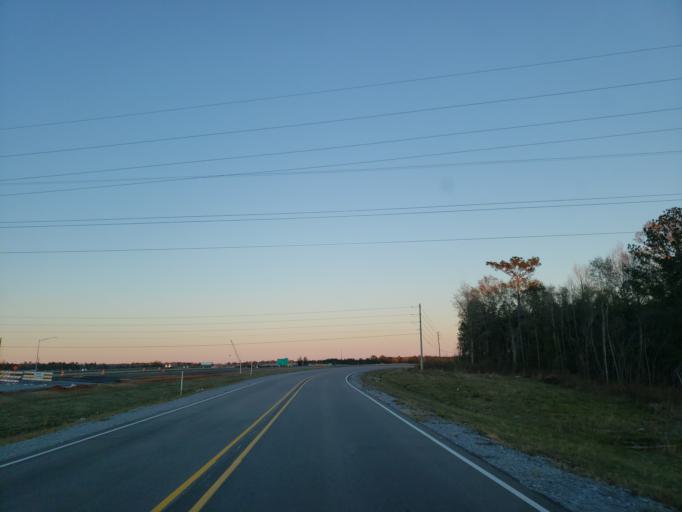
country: US
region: Mississippi
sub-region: Forrest County
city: Glendale
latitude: 31.3759
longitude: -89.3281
